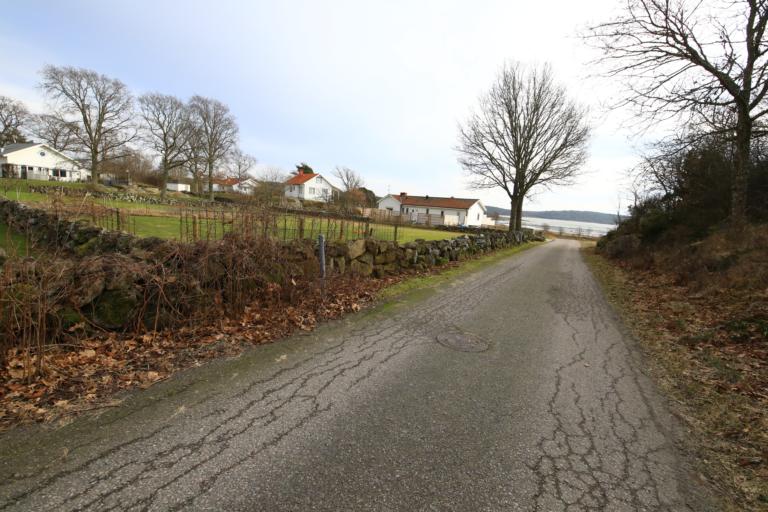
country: SE
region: Halland
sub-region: Varbergs Kommun
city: Varberg
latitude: 57.1929
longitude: 12.2003
